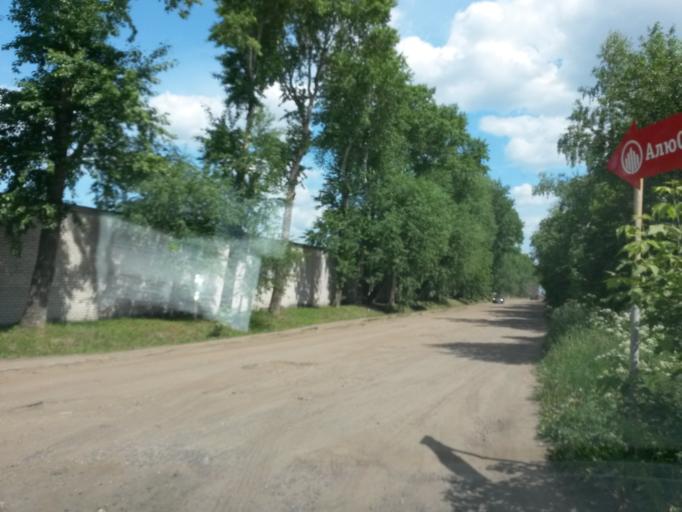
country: RU
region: Jaroslavl
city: Yaroslavl
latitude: 57.5779
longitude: 39.8867
